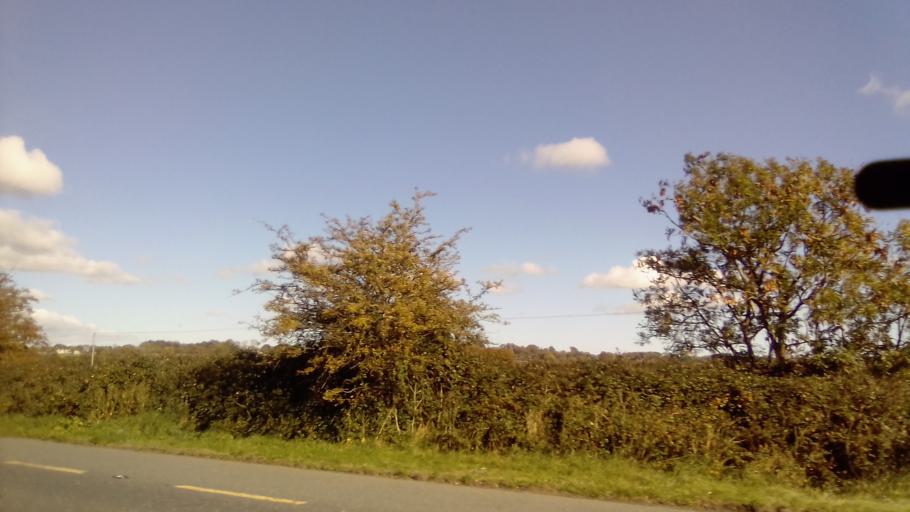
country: IE
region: Leinster
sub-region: An Mhi
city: Ashbourne
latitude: 53.5372
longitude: -6.4247
